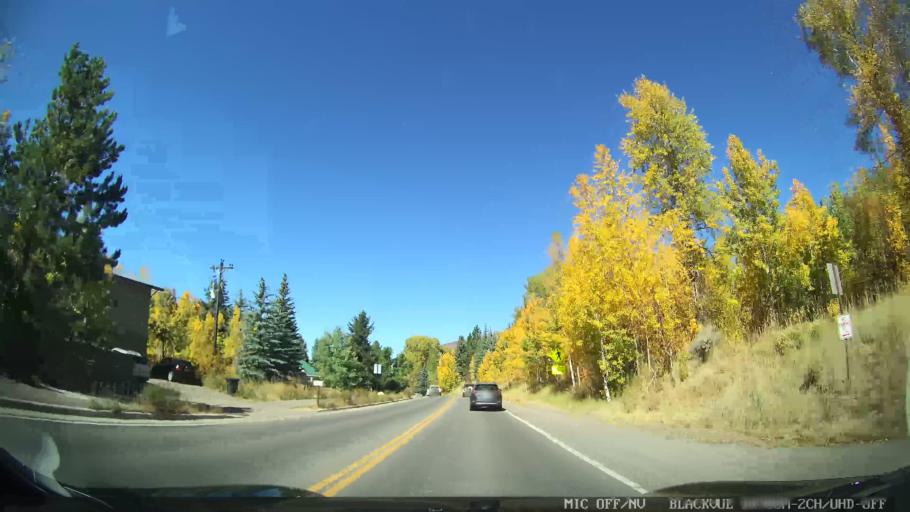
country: US
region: Colorado
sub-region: Pitkin County
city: Aspen
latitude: 39.1843
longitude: -106.8079
